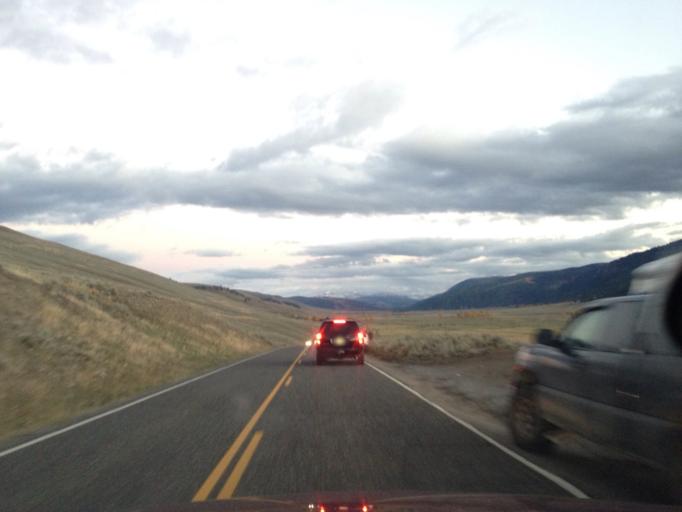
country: US
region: Montana
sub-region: Park County
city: Livingston
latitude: 44.9050
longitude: -110.2478
